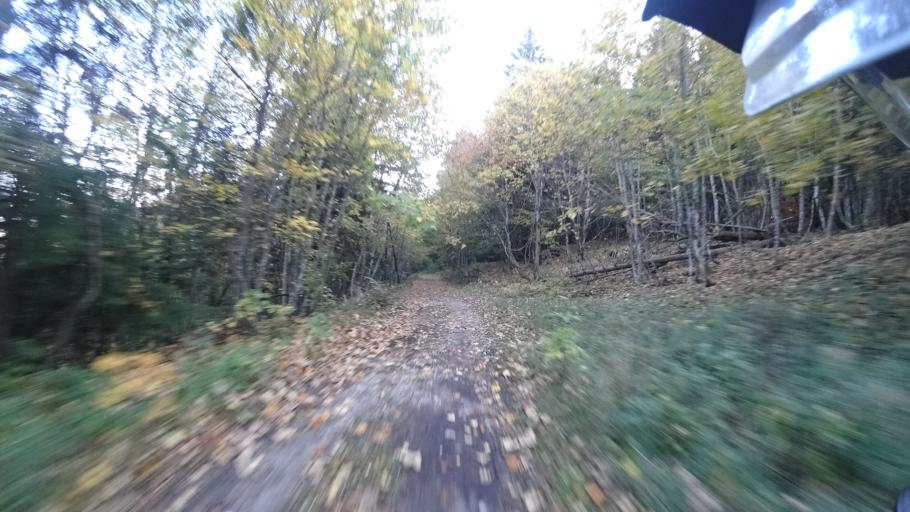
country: HR
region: Karlovacka
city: Plaski
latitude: 44.9684
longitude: 15.4366
